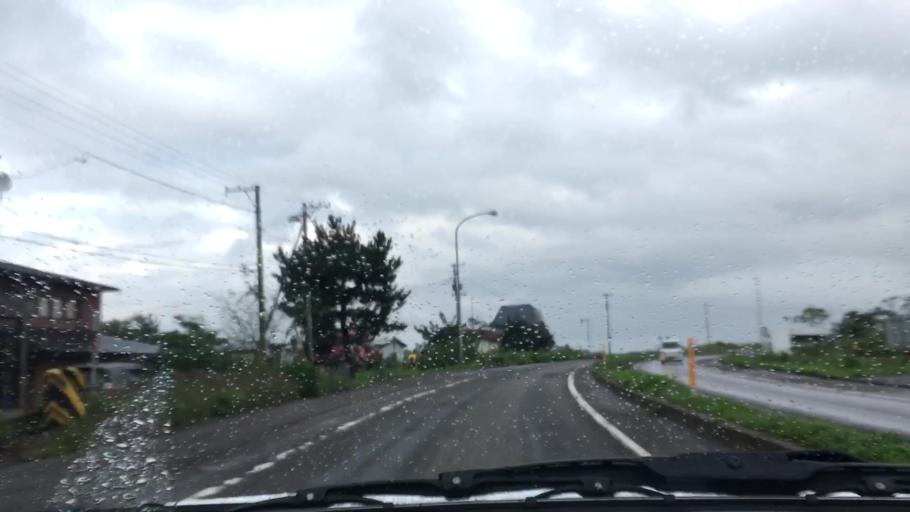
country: JP
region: Hokkaido
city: Nanae
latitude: 42.1886
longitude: 140.4337
